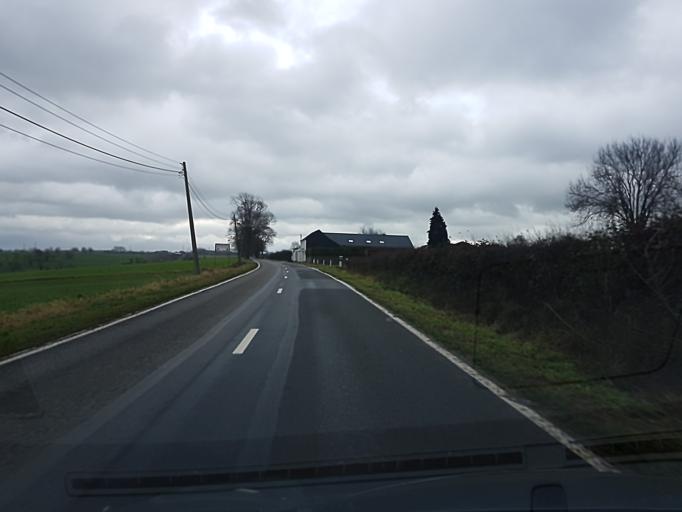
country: BE
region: Wallonia
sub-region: Province de Liege
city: Herve
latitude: 50.6687
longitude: 5.7759
